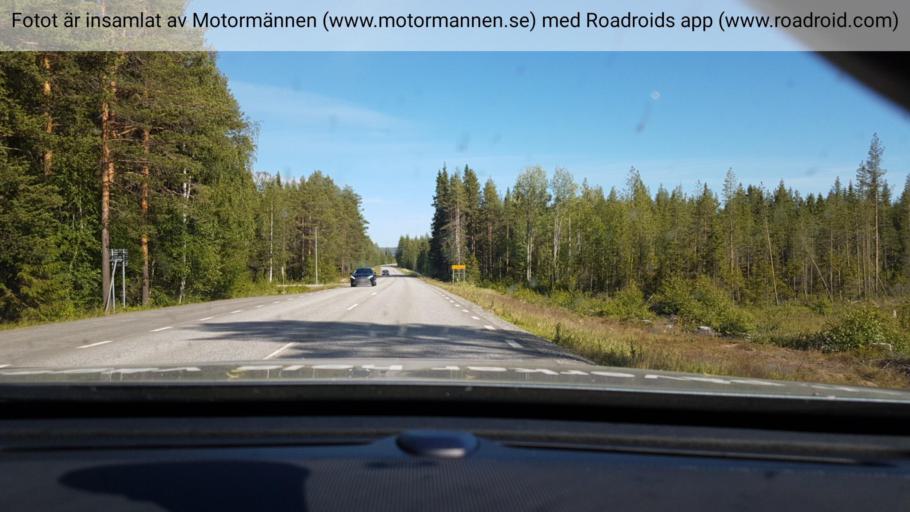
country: SE
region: Vaesterbotten
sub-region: Lycksele Kommun
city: Lycksele
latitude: 64.6466
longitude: 18.4893
